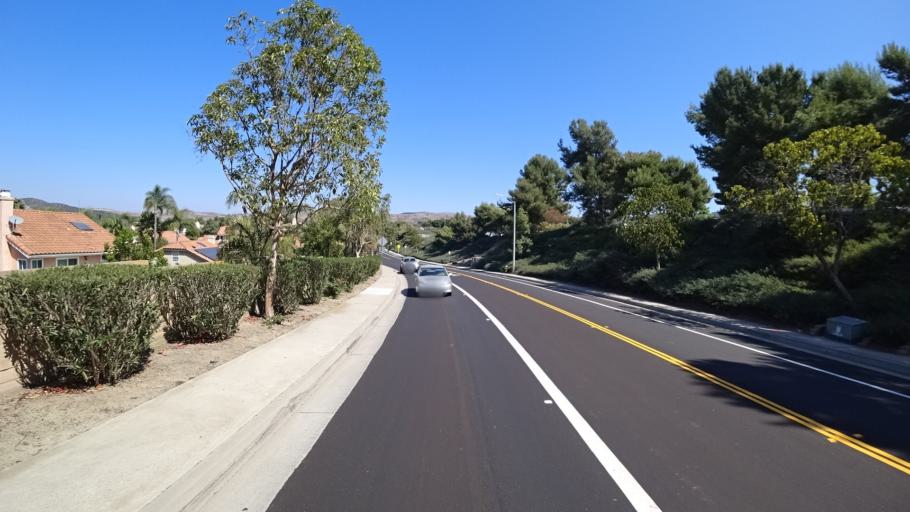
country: US
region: California
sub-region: Orange County
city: San Clemente
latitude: 33.4668
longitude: -117.6269
